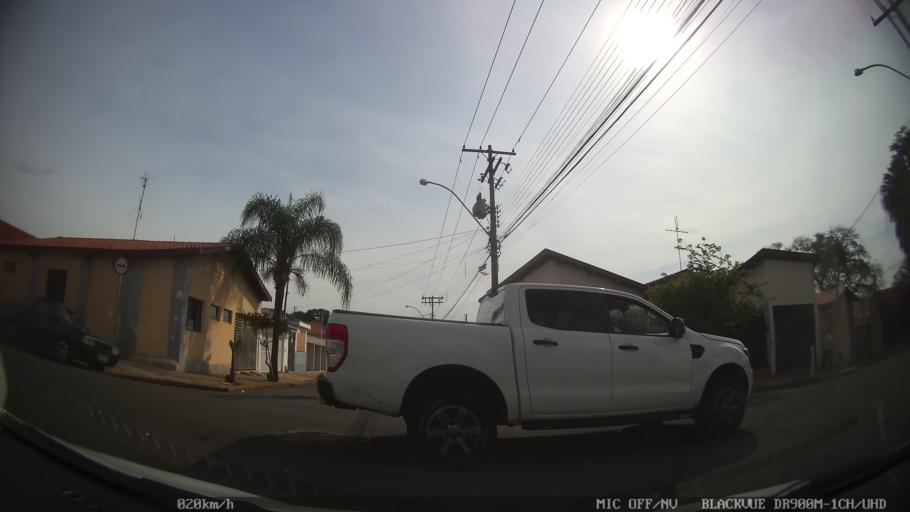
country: BR
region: Sao Paulo
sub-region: Piracicaba
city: Piracicaba
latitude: -22.7365
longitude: -47.6570
